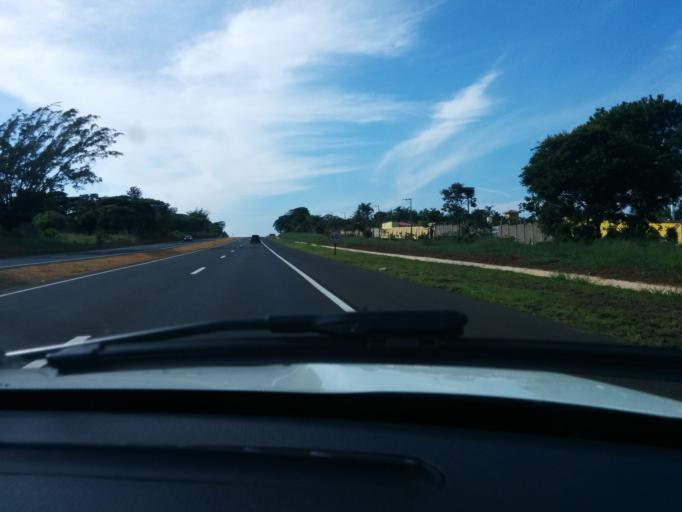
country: BR
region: Sao Paulo
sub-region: Franca
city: Franca
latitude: -20.4531
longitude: -47.4177
